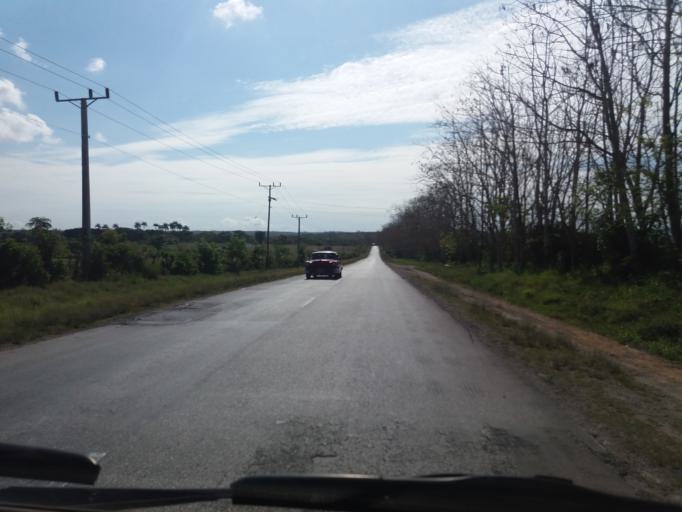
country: CU
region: Cienfuegos
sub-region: Municipio de Cienfuegos
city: Cienfuegos
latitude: 22.1655
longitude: -80.3799
